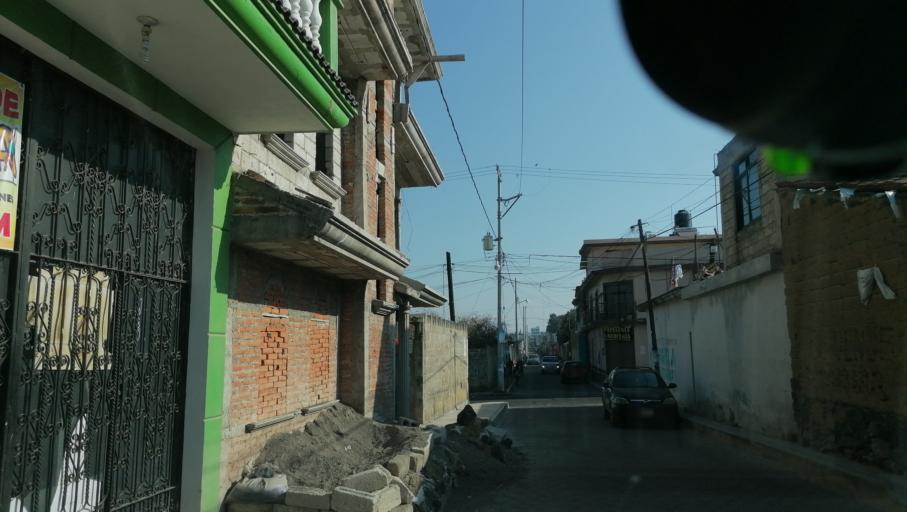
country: MX
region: Puebla
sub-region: Tianguismanalco
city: San Martin Tlapala
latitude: 18.9737
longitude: -98.4506
